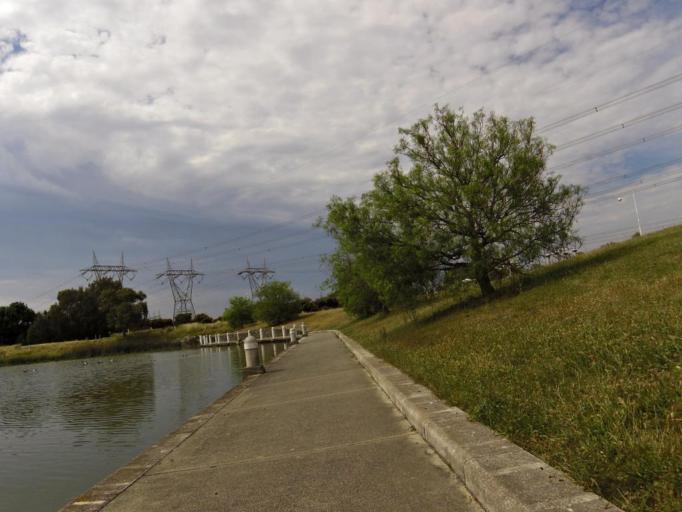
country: AU
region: Victoria
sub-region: Whittlesea
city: Mill Park
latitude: -37.6406
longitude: 145.0688
